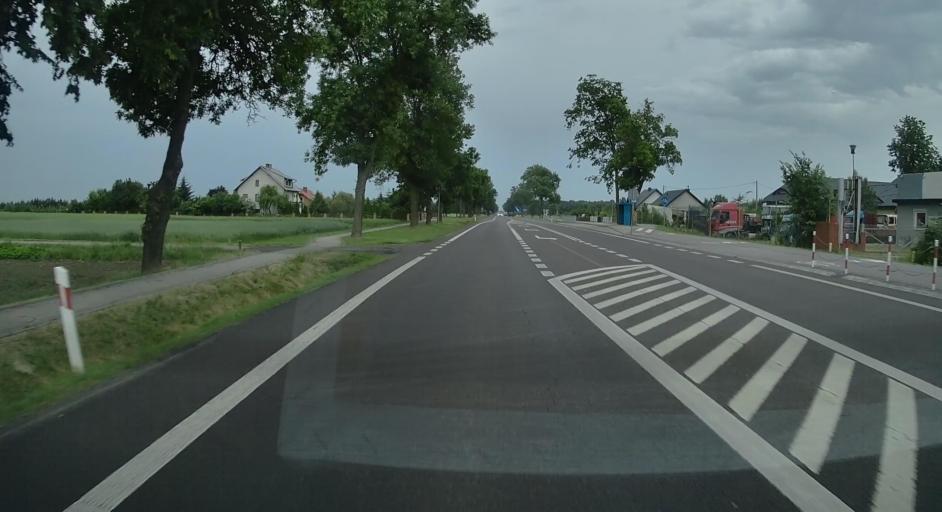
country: PL
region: Lublin Voivodeship
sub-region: Powiat bialski
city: Rzeczyca
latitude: 52.0181
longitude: 22.7274
